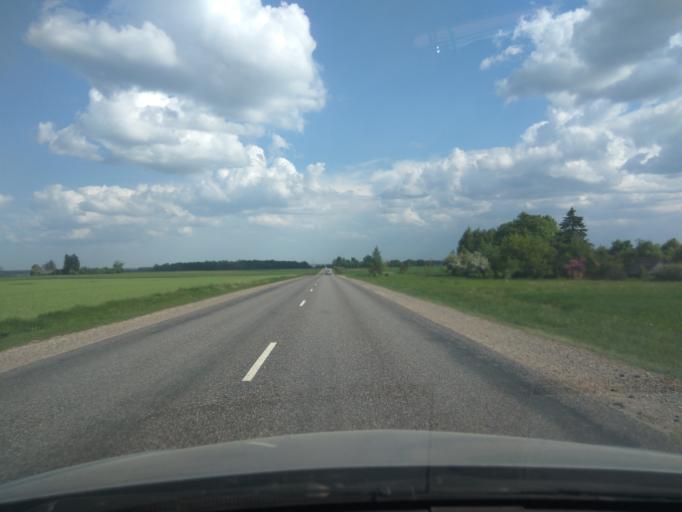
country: LV
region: Kuldigas Rajons
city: Kuldiga
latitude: 56.9946
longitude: 21.9064
